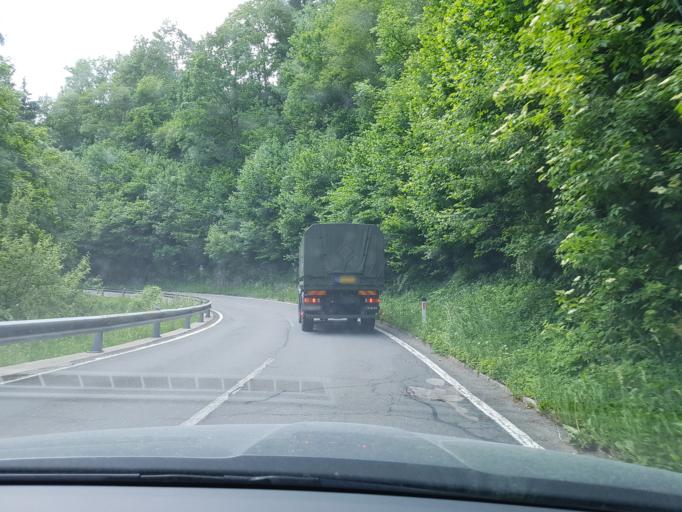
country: AT
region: Carinthia
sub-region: Politischer Bezirk Villach Land
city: Feld am See
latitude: 46.7977
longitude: 13.7458
